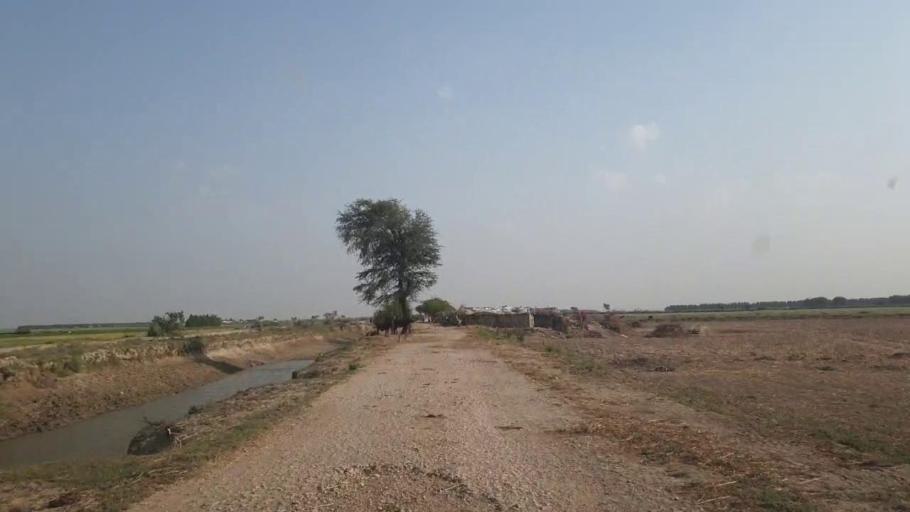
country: PK
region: Sindh
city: Kario
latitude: 24.5924
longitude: 68.5560
